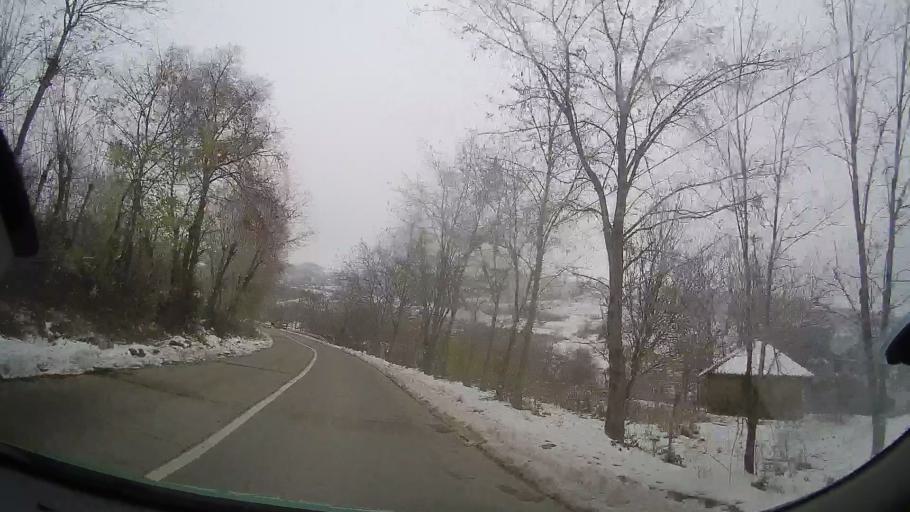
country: RO
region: Vrancea
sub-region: Comuna Boghesti
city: Boghesti
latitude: 46.1961
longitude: 27.4427
